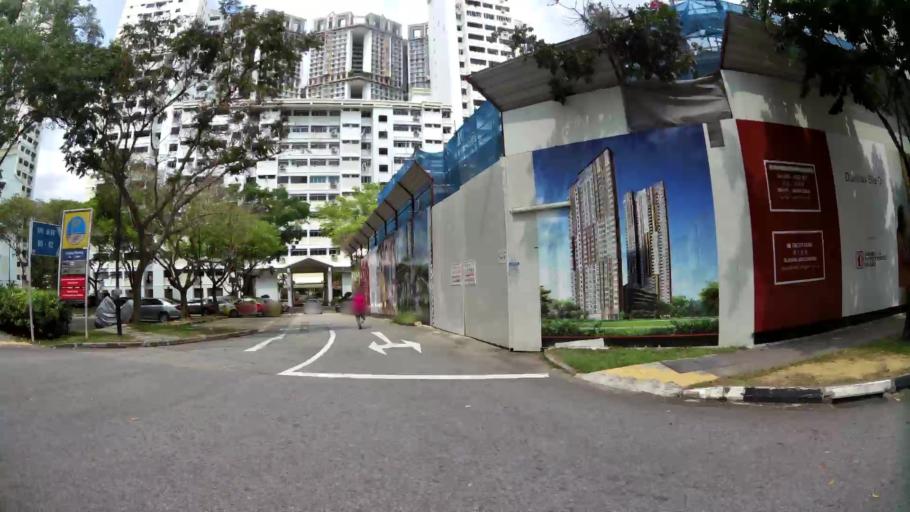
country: SG
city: Singapore
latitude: 1.2940
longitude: 103.8098
